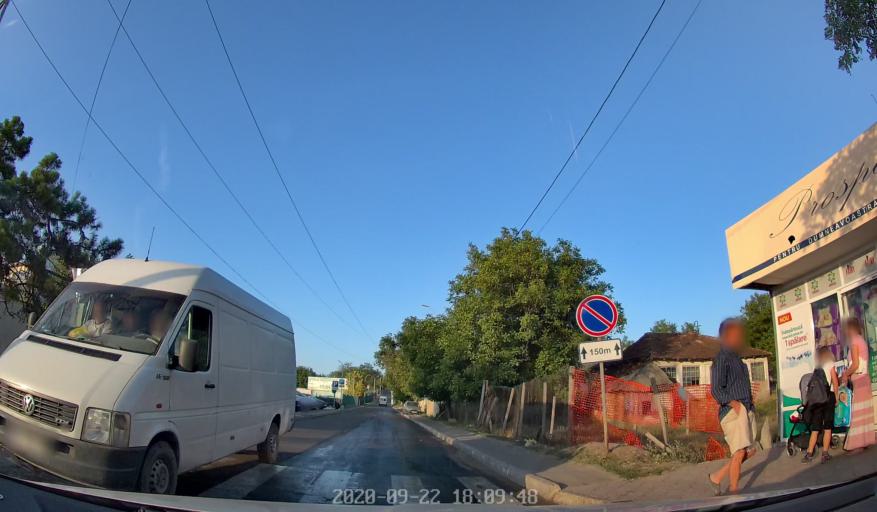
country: MD
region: Laloveni
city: Ialoveni
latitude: 46.9440
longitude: 28.7771
